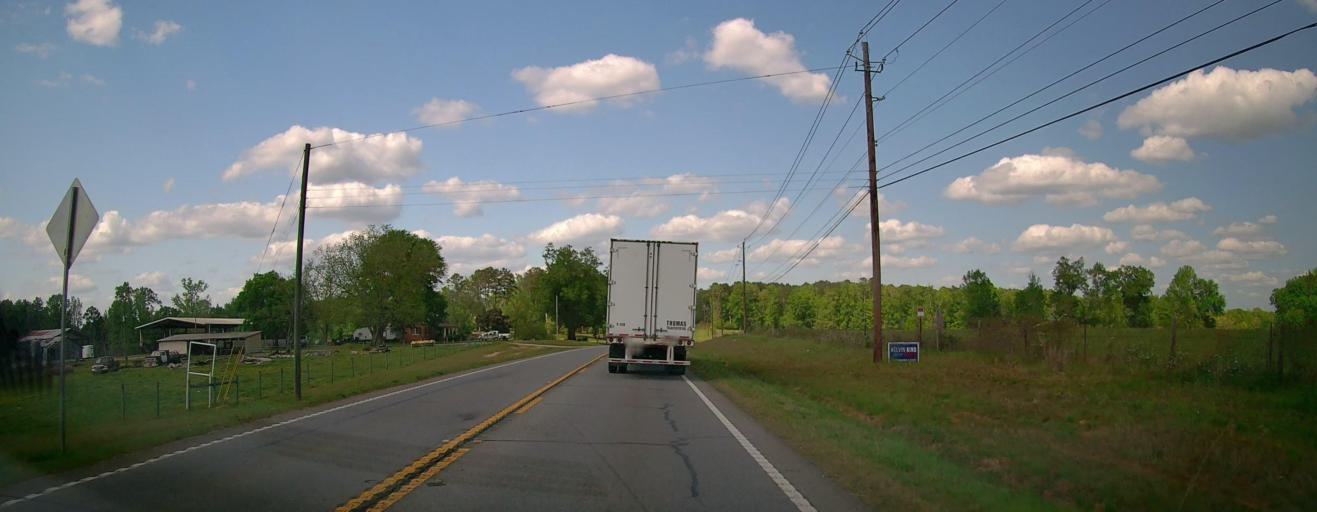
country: US
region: Georgia
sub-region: Greene County
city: Greensboro
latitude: 33.5140
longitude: -83.2261
